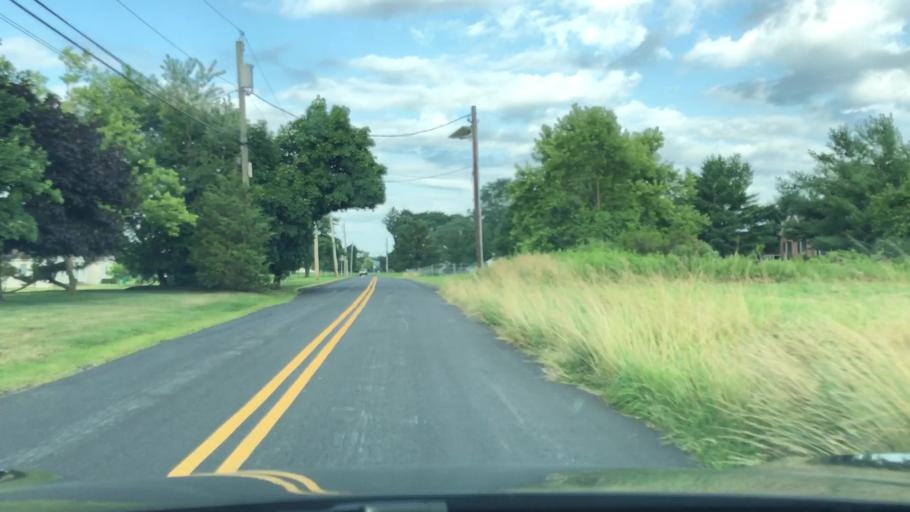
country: US
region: New Jersey
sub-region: Mercer County
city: Pennington
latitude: 40.3389
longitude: -74.8124
